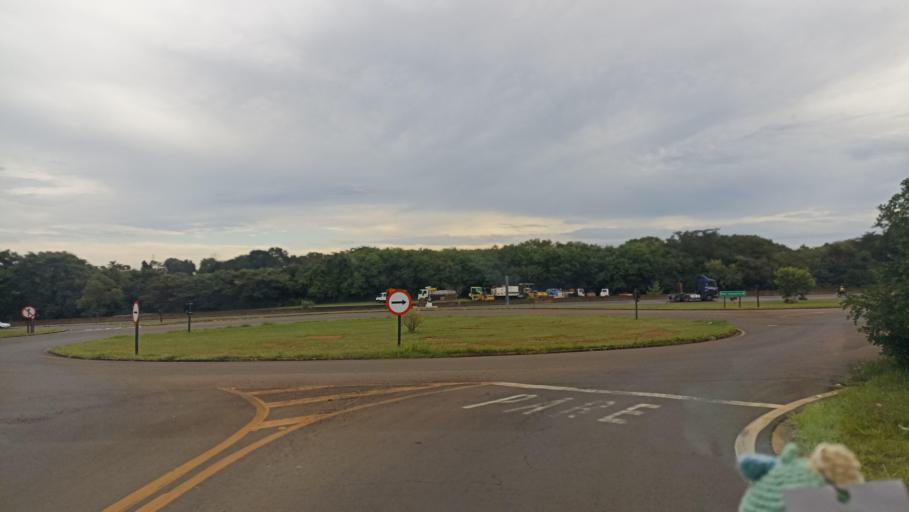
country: BR
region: Sao Paulo
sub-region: Jaboticabal
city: Jaboticabal
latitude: -21.2641
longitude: -48.3419
